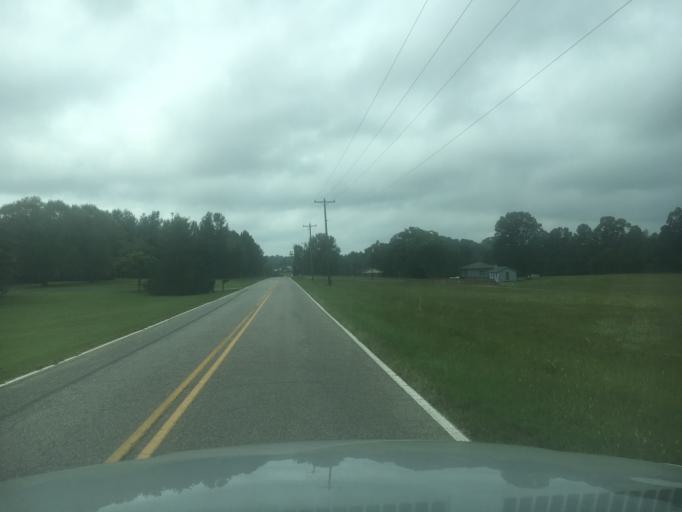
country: US
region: South Carolina
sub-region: Spartanburg County
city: Landrum
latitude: 35.1530
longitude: -82.1015
